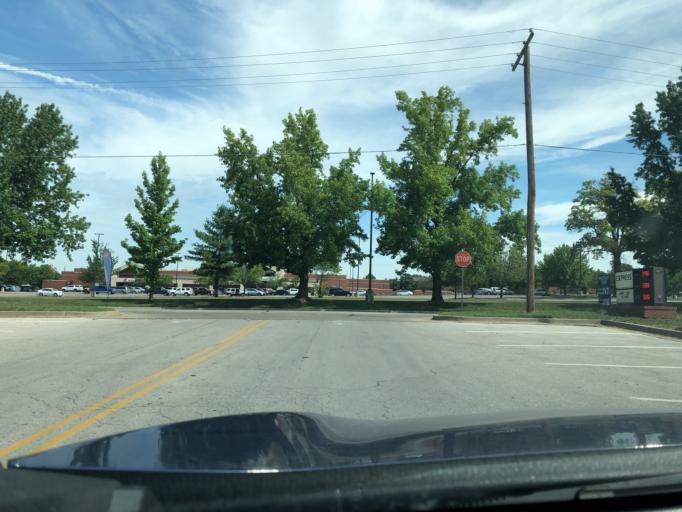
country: US
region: Kansas
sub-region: Leavenworth County
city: Leavenworth
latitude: 39.3380
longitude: -94.9244
